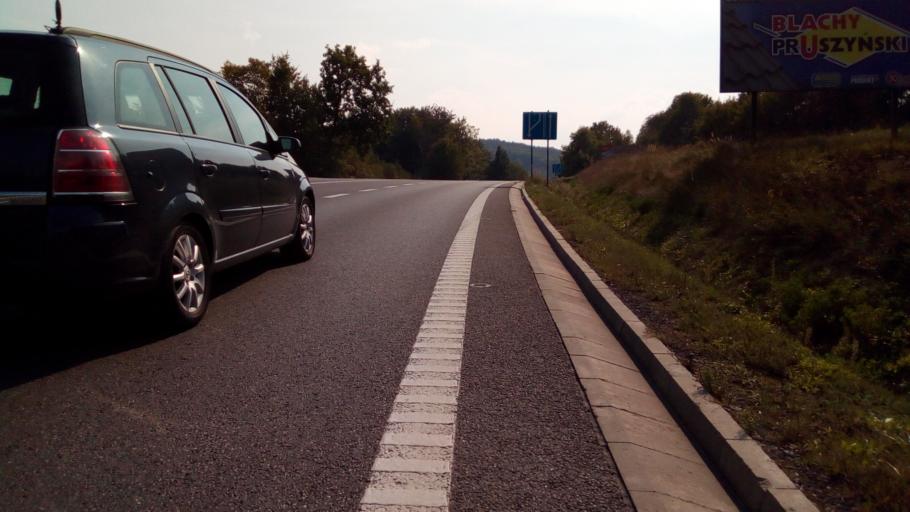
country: PL
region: Subcarpathian Voivodeship
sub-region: Powiat strzyzowski
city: Jawornik
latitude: 49.8375
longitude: 21.8882
